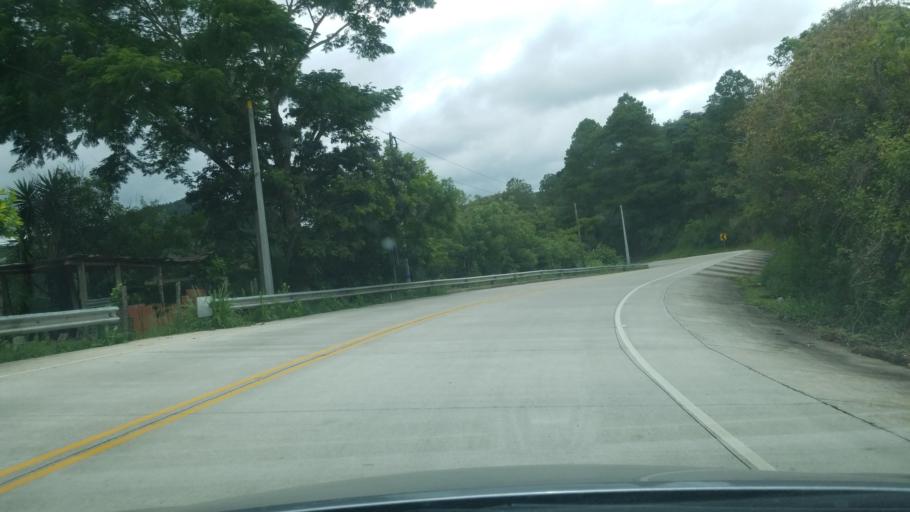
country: HN
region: Copan
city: San Jeronimo
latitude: 14.9336
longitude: -88.9318
